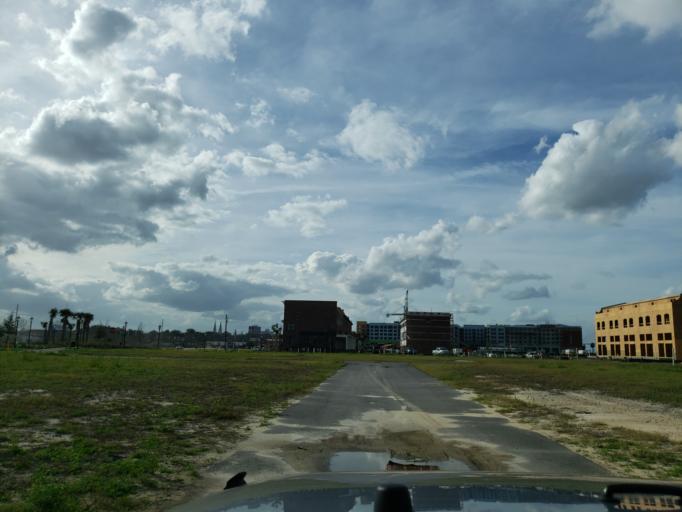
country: US
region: Georgia
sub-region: Chatham County
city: Savannah
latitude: 32.0765
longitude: -81.0749
